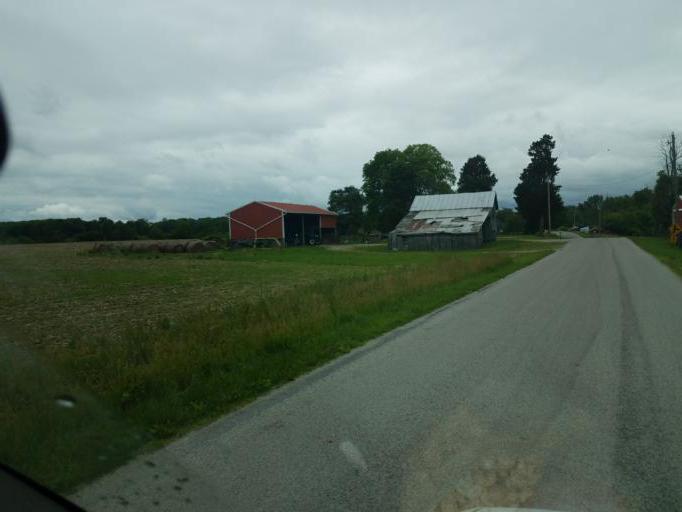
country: US
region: Ohio
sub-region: Morrow County
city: Cardington
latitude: 40.5292
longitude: -82.8770
